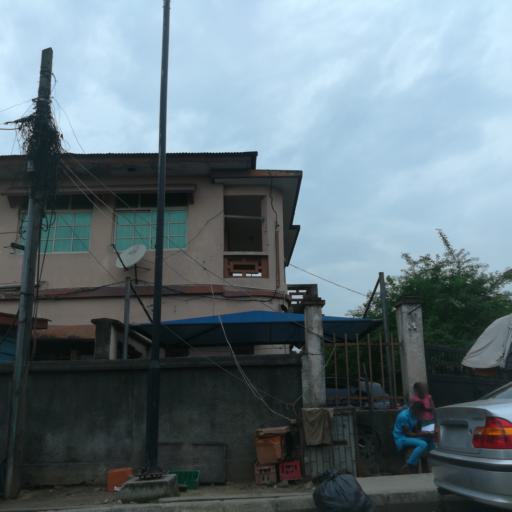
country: NG
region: Lagos
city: Makoko
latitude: 6.5003
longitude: 3.3795
